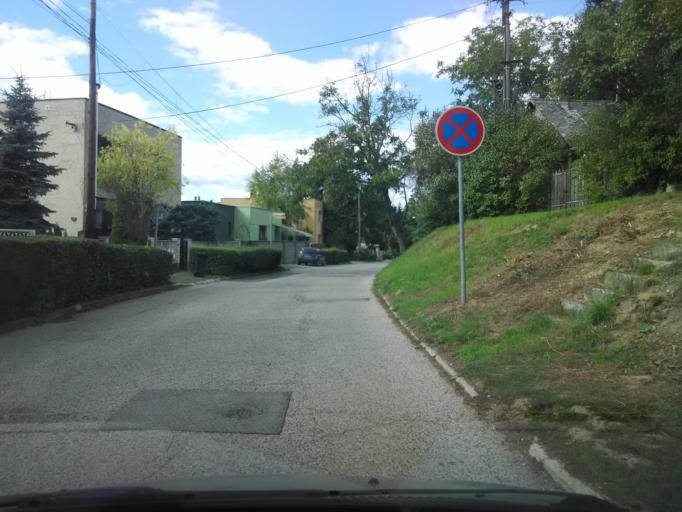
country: SK
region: Nitriansky
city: Levice
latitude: 48.2119
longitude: 18.6234
